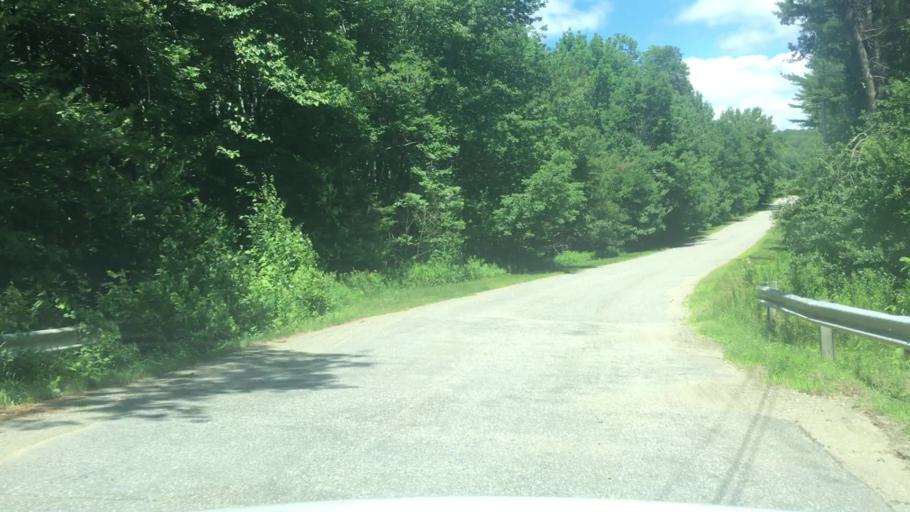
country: US
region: Maine
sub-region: Kennebec County
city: Albion
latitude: 44.4769
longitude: -69.3001
